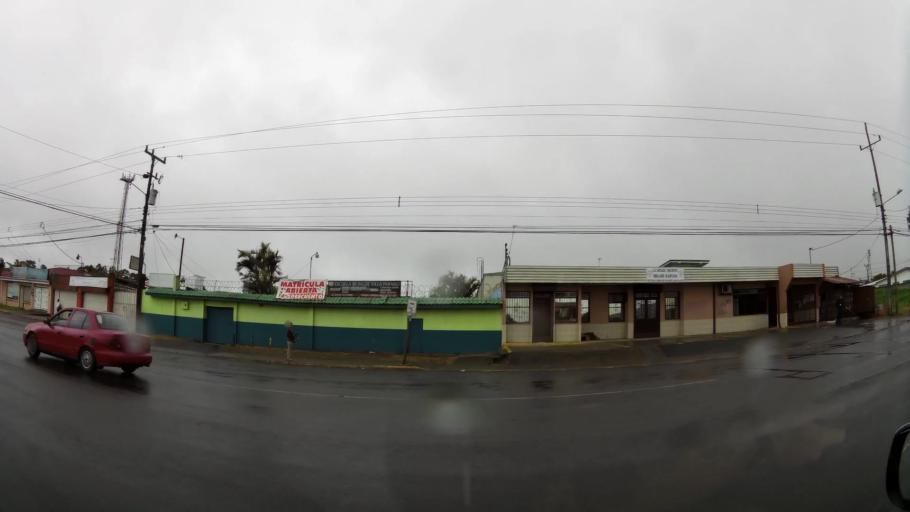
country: CR
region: Cartago
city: Paraiso
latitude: 9.8426
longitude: -83.8808
